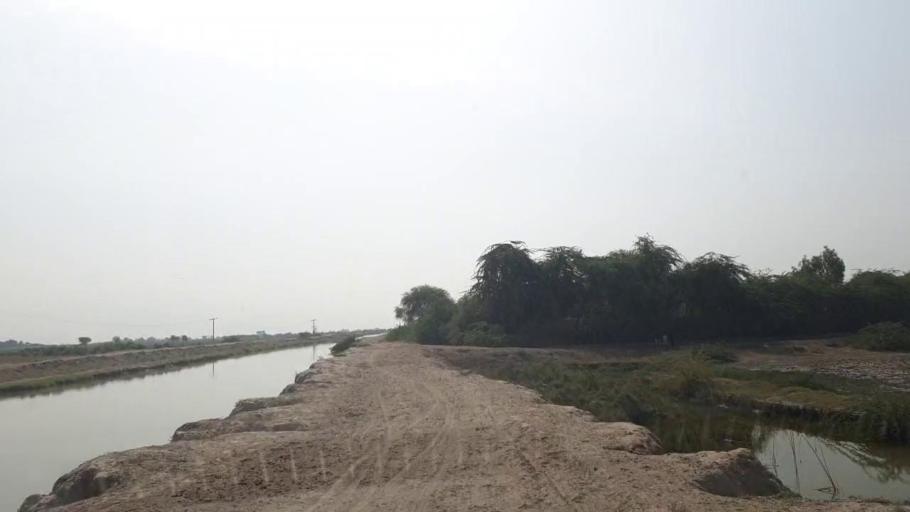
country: PK
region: Sindh
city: Badin
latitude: 24.5518
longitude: 68.8498
